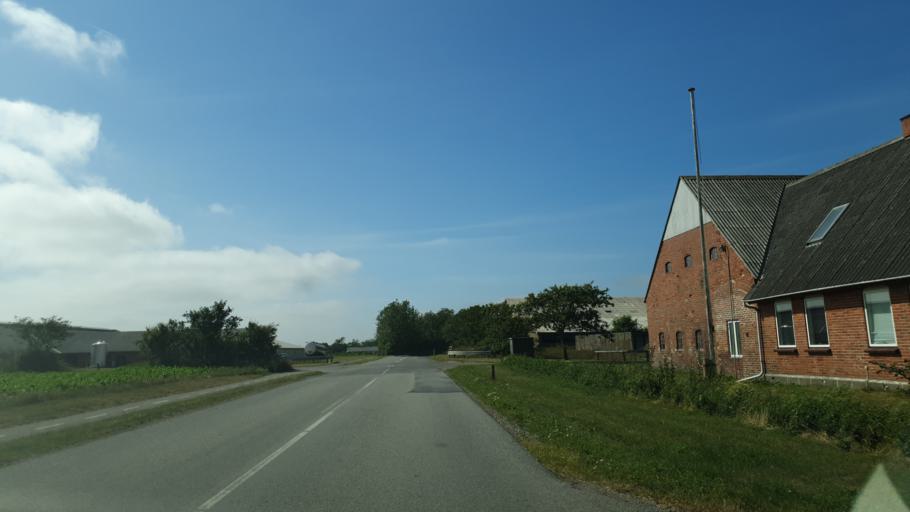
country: DK
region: Central Jutland
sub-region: Ringkobing-Skjern Kommune
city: Ringkobing
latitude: 56.0357
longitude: 8.3248
